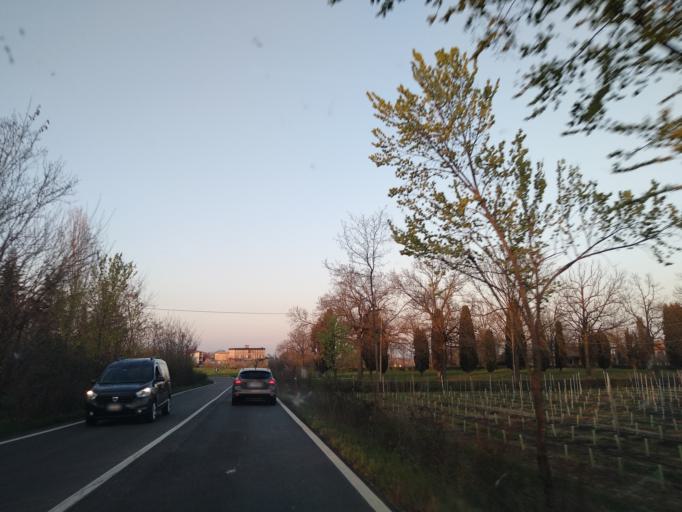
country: IT
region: Emilia-Romagna
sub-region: Provincia di Reggio Emilia
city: Forche
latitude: 44.6359
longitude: 10.5771
